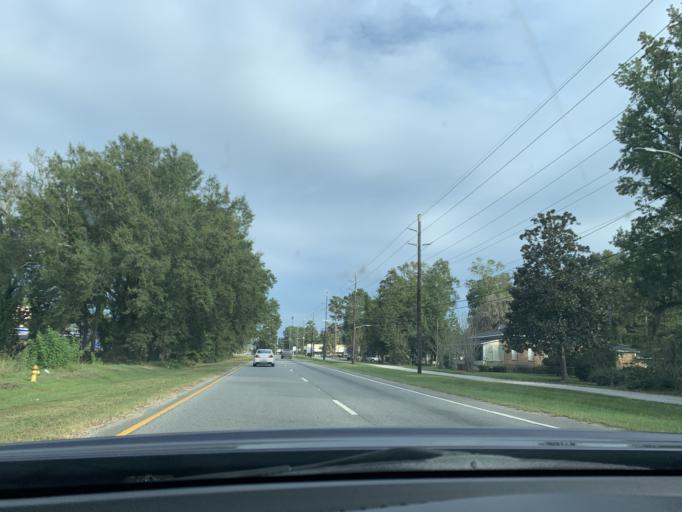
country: US
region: Georgia
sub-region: Chatham County
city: Pooler
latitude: 32.1144
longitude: -81.2462
